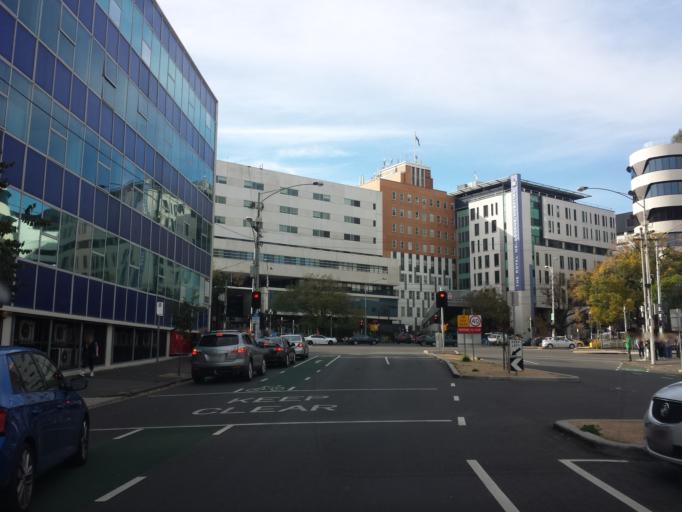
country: AU
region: Victoria
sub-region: Melbourne
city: North Melbourne
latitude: -37.8000
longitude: 144.9546
